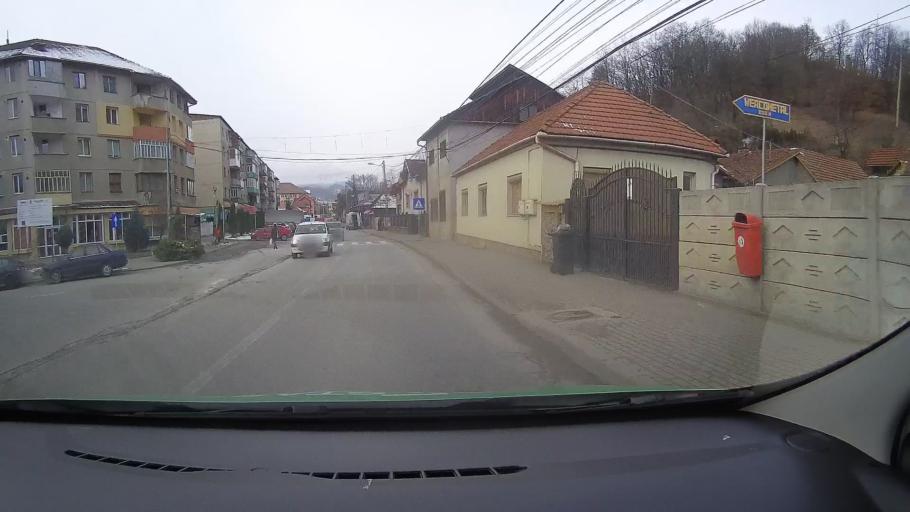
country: RO
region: Alba
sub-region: Oras Zlatna
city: Zlatna
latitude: 46.1088
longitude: 23.2307
